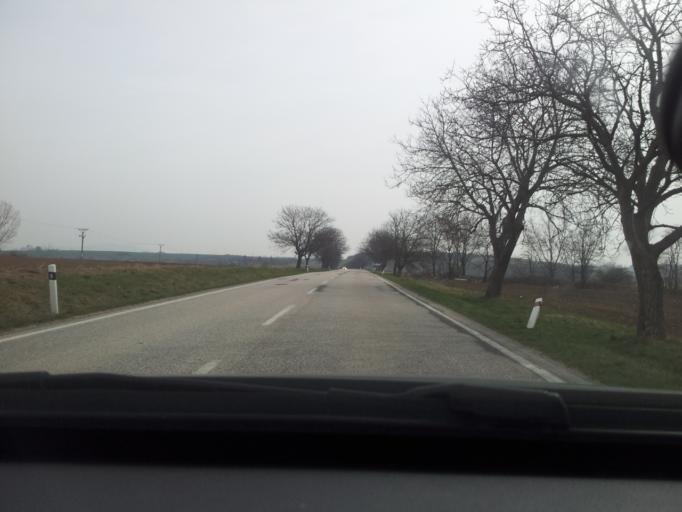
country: SK
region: Trnavsky
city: Hlohovec
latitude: 48.3607
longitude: 17.9229
